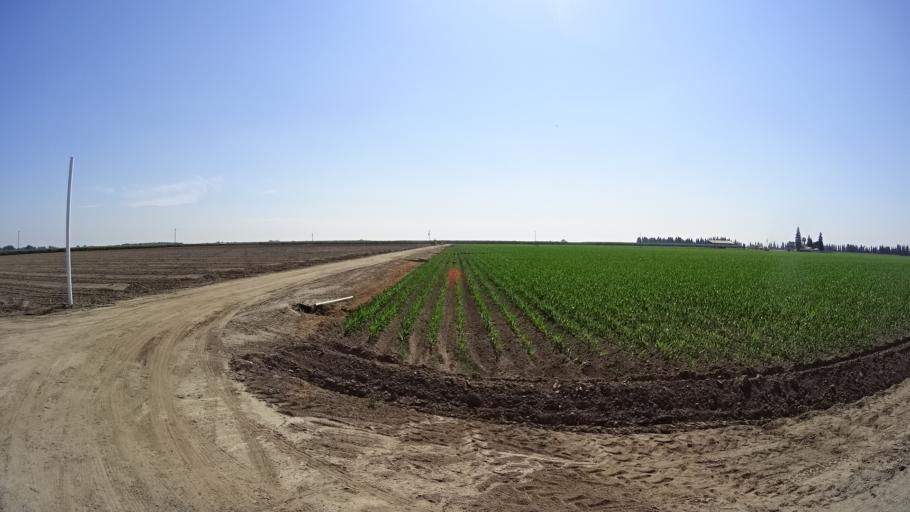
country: US
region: California
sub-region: Kings County
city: Lucerne
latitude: 36.4195
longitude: -119.5824
